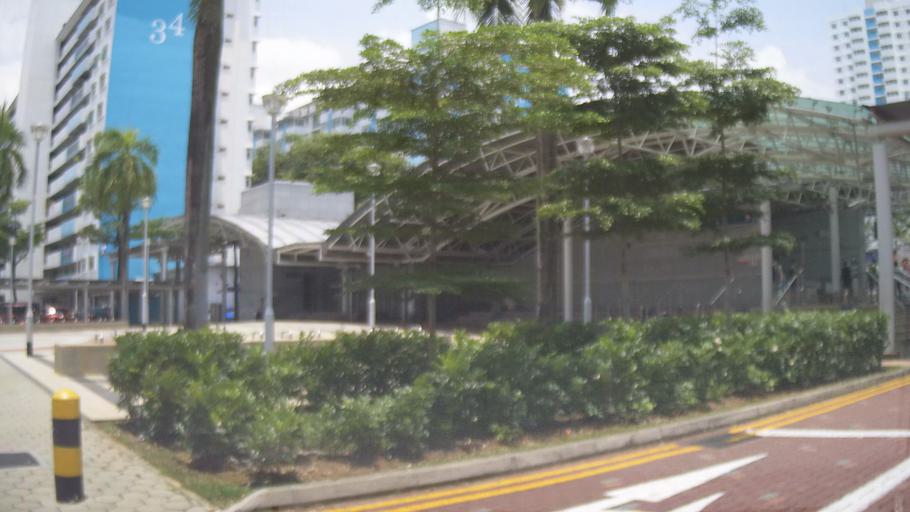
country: SG
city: Singapore
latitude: 1.3193
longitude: 103.8617
